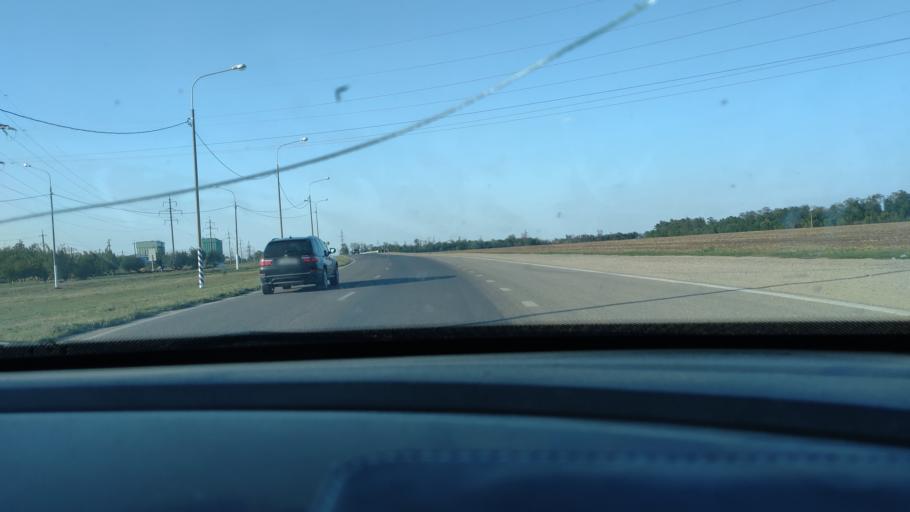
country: RU
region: Krasnodarskiy
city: Timashevsk
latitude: 45.6098
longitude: 38.9872
